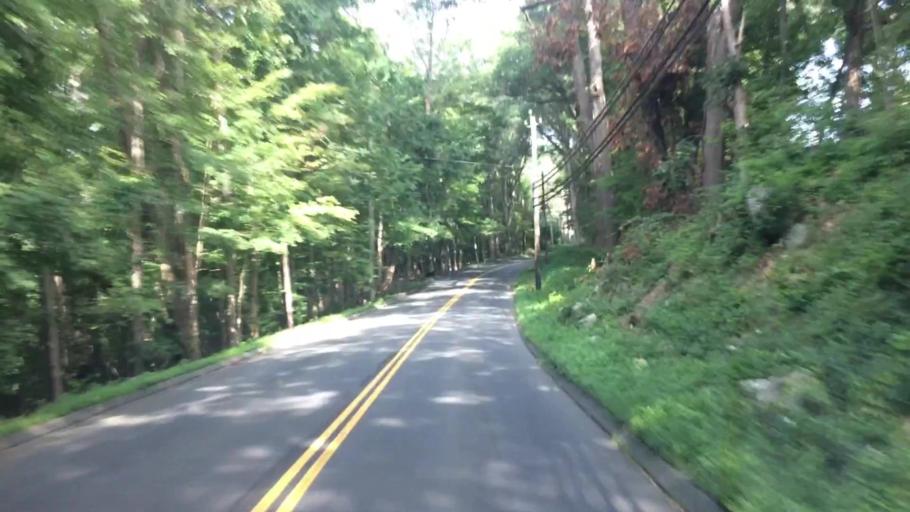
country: US
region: Connecticut
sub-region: Fairfield County
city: Danbury
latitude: 41.4033
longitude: -73.4756
